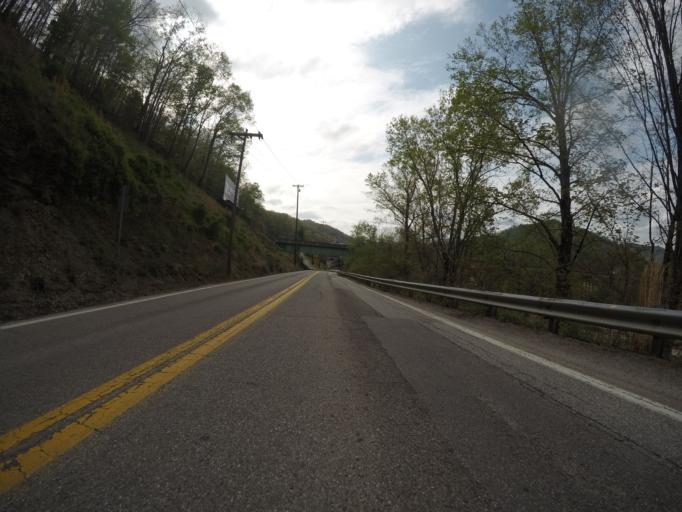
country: US
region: West Virginia
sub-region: Boone County
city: Madison
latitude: 38.0865
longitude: -81.8389
